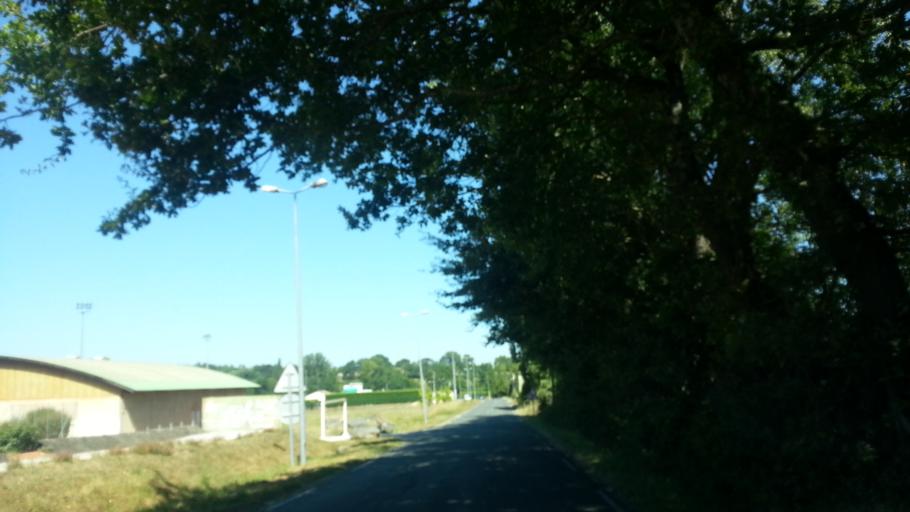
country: FR
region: Aquitaine
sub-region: Departement de la Gironde
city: Martillac
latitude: 44.6897
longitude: -0.5095
